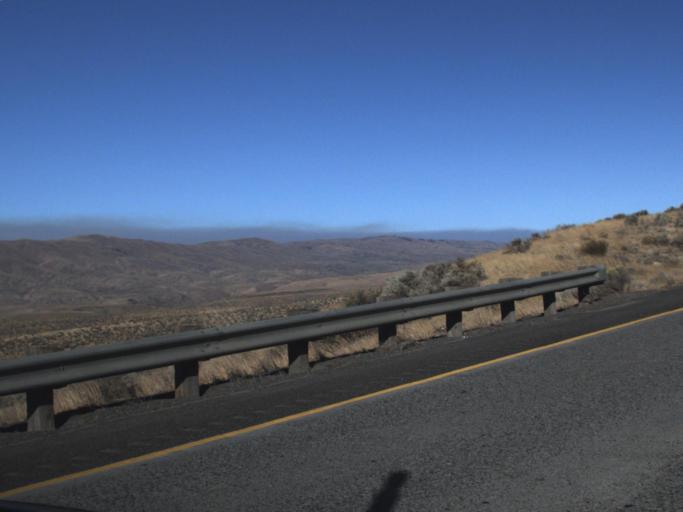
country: US
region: Washington
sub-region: Kittitas County
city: Kittitas
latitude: 46.8640
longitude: -120.4015
